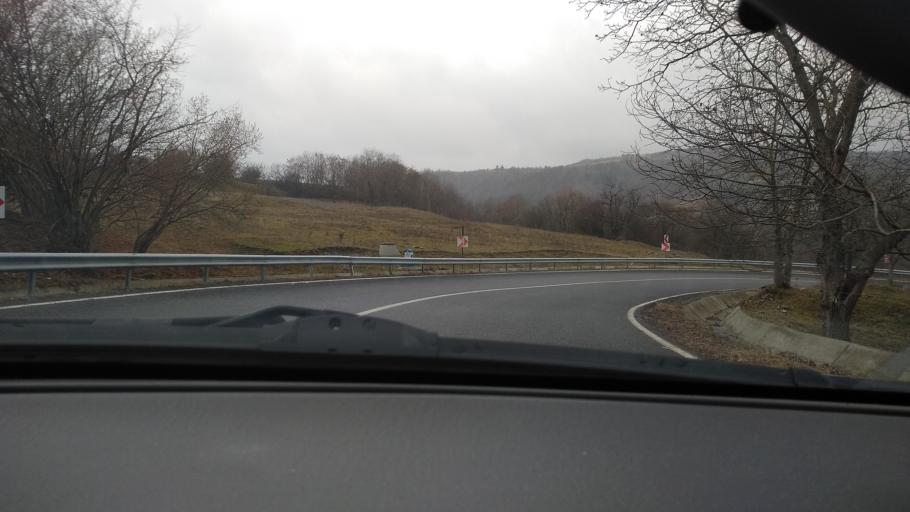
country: RO
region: Mures
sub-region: Comuna Magherani
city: Magherani
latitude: 46.5800
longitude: 24.9456
